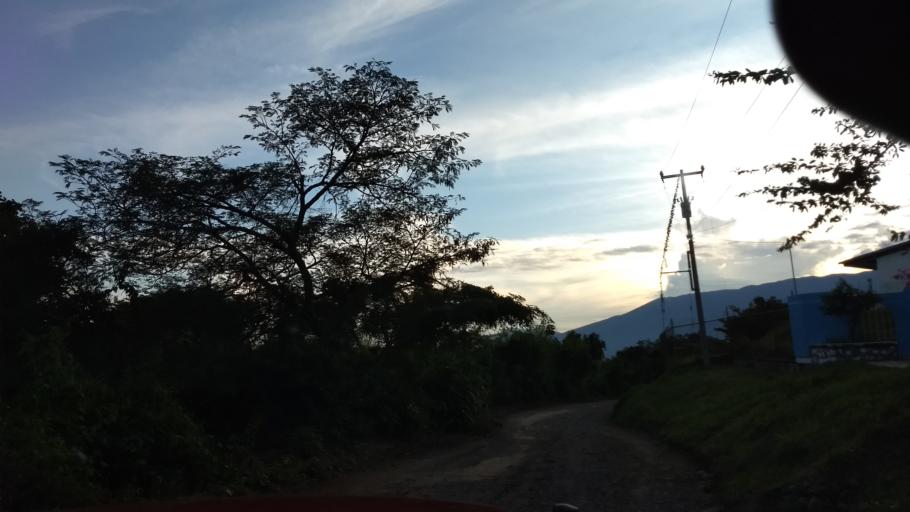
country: MX
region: Jalisco
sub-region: San Gabriel
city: Alista
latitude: 19.4997
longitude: -103.7672
